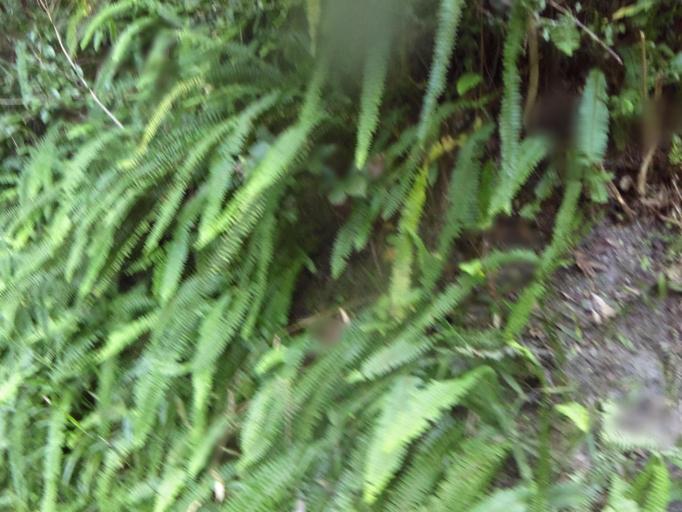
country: US
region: Florida
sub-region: Putnam County
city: Palatka
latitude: 29.6345
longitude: -81.6459
